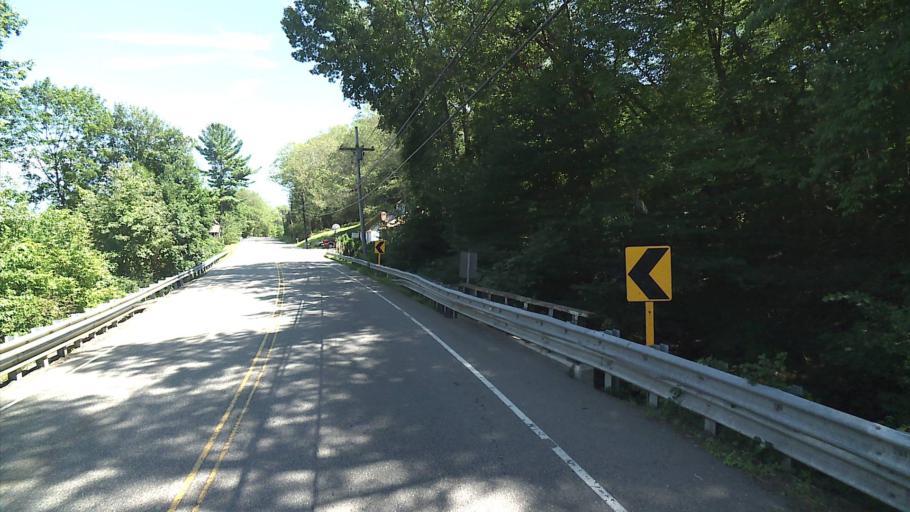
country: US
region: Connecticut
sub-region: New London County
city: Baltic
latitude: 41.6075
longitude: -72.0671
